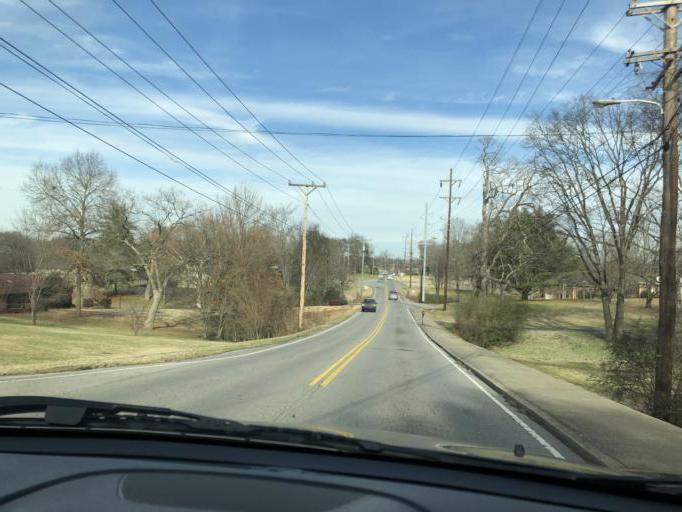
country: US
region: Tennessee
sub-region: Davidson County
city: Lakewood
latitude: 36.1799
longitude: -86.6780
